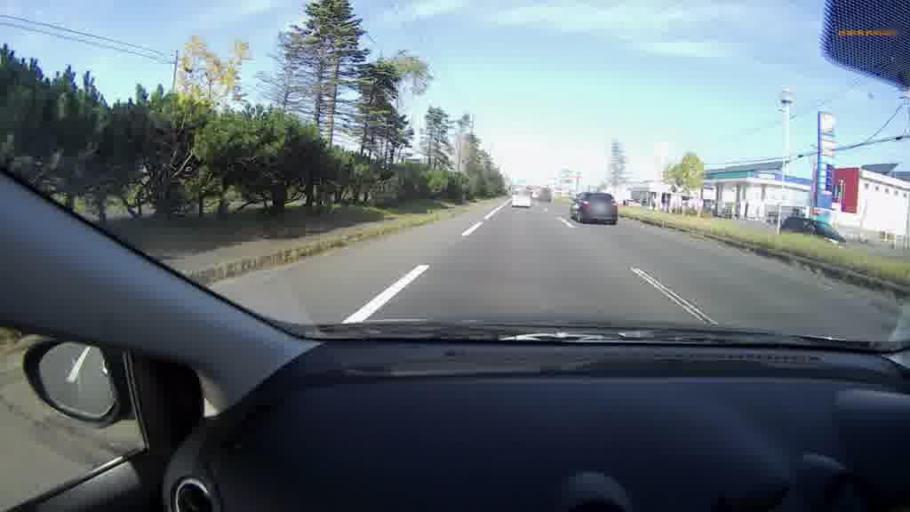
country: JP
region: Hokkaido
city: Kushiro
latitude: 43.0069
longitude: 144.4144
